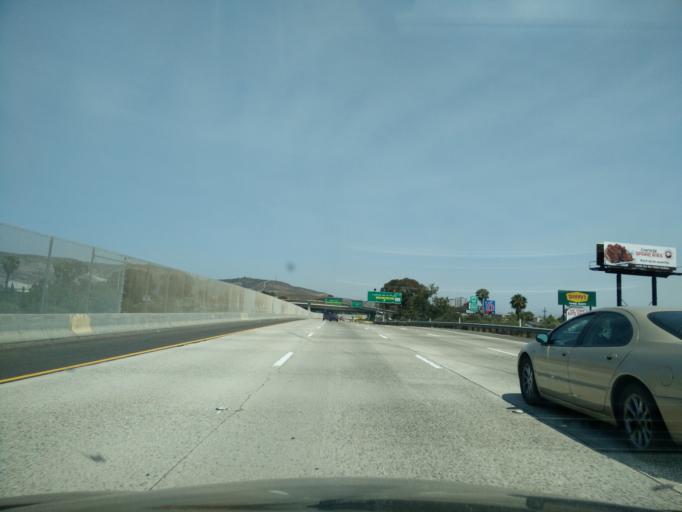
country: MX
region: Baja California
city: Tijuana
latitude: 32.5511
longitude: -117.0449
